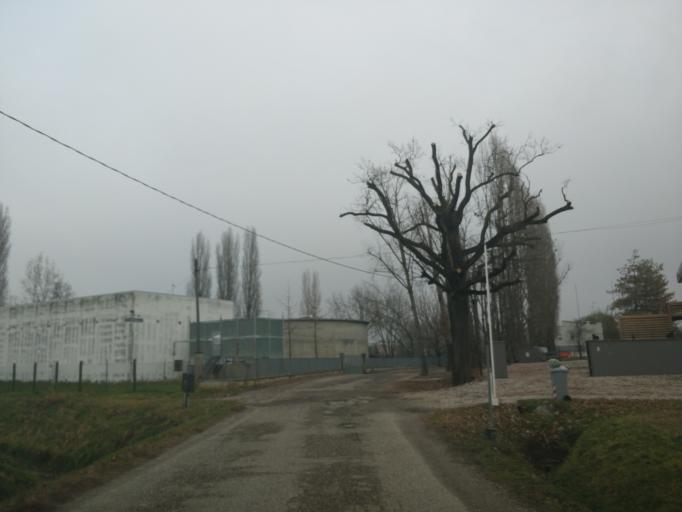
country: IT
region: Emilia-Romagna
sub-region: Provincia di Ferrara
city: Cento
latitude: 44.7150
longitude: 11.2821
